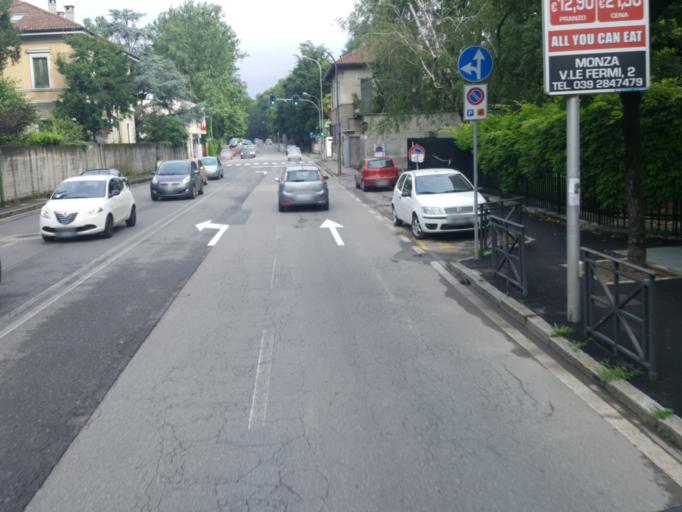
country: IT
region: Lombardy
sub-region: Provincia di Monza e Brianza
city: Monza
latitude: 45.5891
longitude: 9.2838
